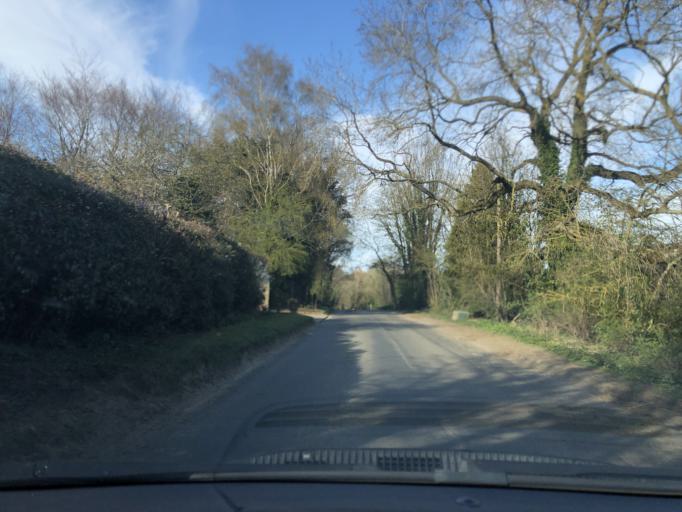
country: GB
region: England
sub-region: Oxfordshire
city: Bloxham
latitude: 52.0300
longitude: -1.4152
